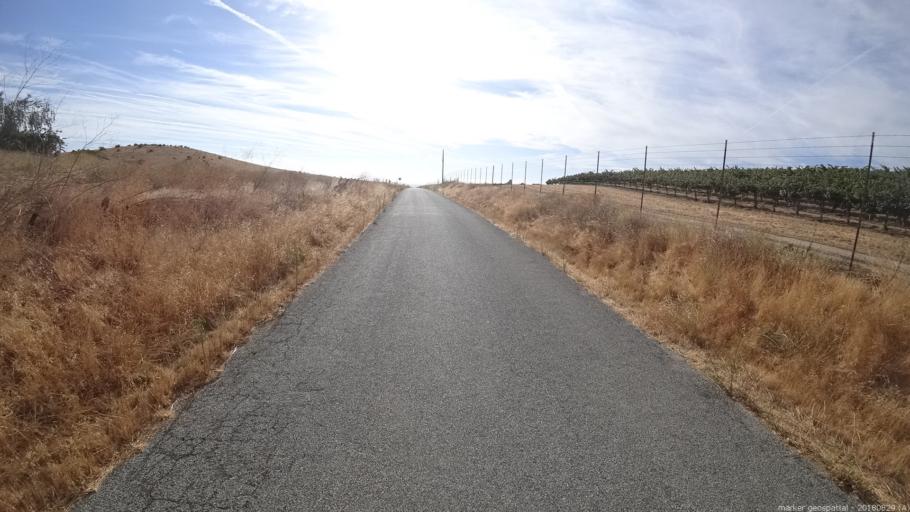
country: US
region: California
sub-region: Monterey County
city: King City
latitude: 36.0189
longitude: -120.9481
